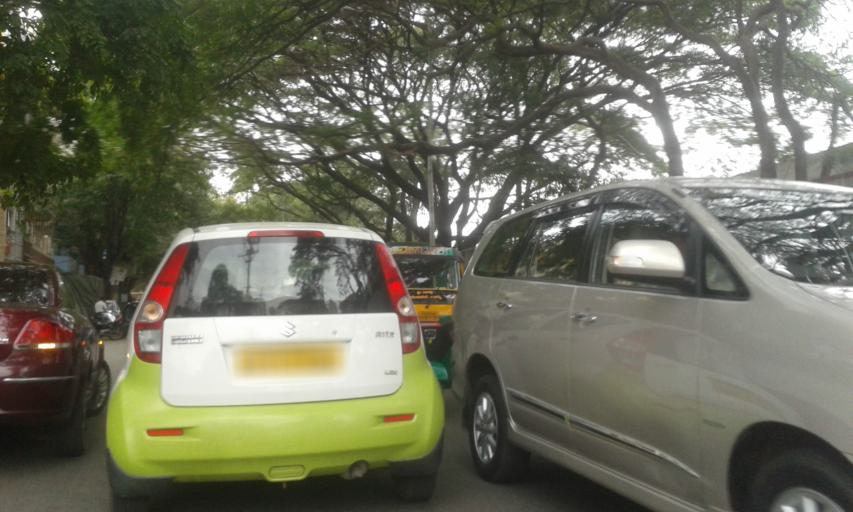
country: IN
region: Karnataka
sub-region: Bangalore Urban
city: Bangalore
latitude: 12.9205
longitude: 77.5968
